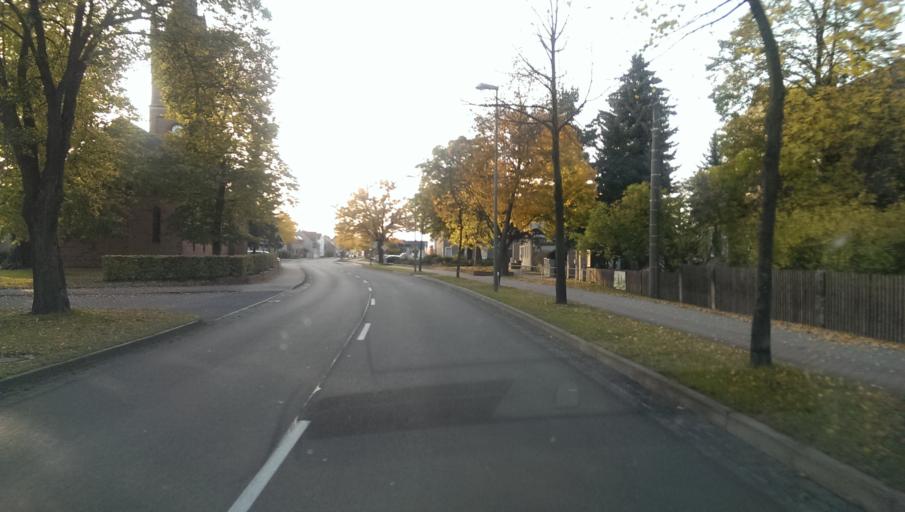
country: DE
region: Saxony-Anhalt
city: Holzdorf
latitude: 51.7787
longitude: 13.1300
